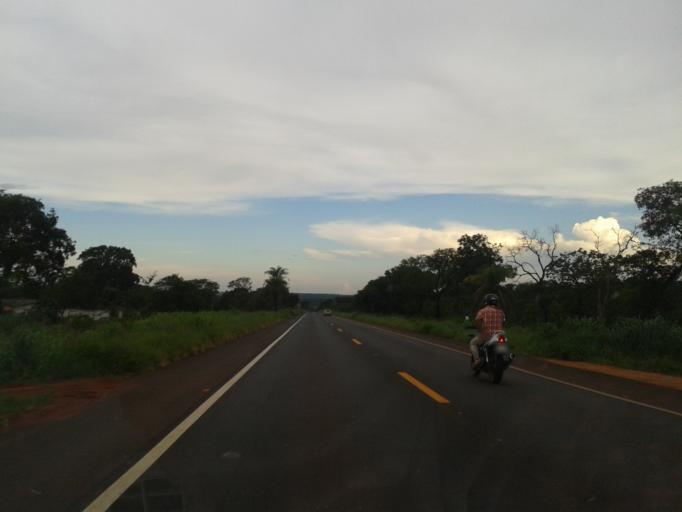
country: BR
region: Minas Gerais
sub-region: Santa Vitoria
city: Santa Vitoria
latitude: -18.8816
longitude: -50.1376
